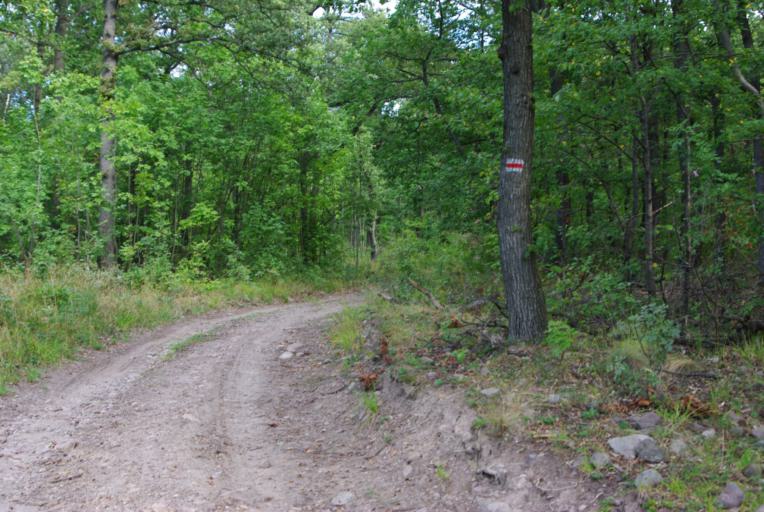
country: HU
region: Pest
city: Csobanka
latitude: 47.6740
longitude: 18.9630
